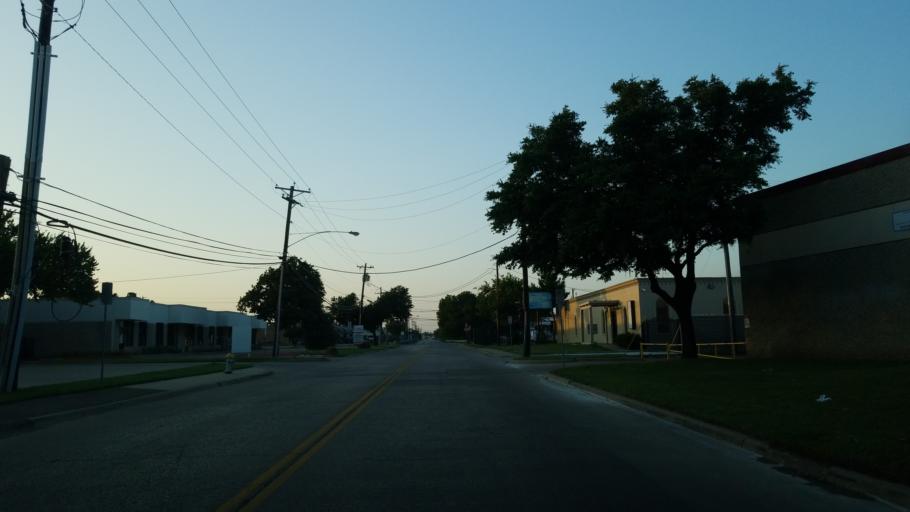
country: US
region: Texas
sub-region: Dallas County
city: Farmers Branch
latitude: 32.8851
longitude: -96.8904
